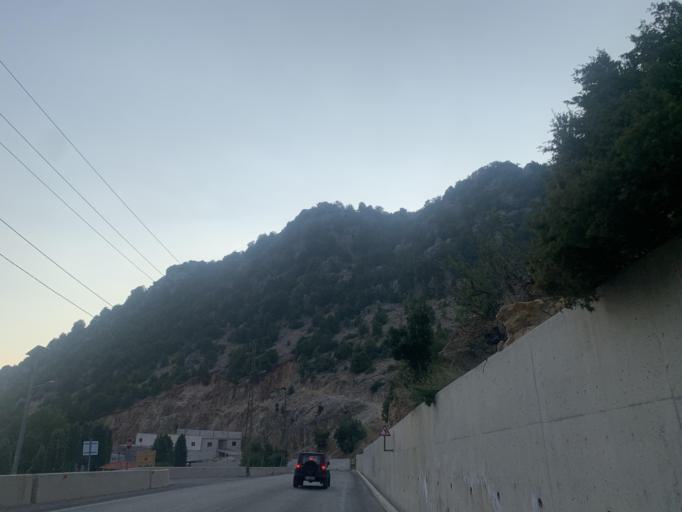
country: LB
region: Liban-Nord
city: Amioun
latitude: 34.1357
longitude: 35.8253
